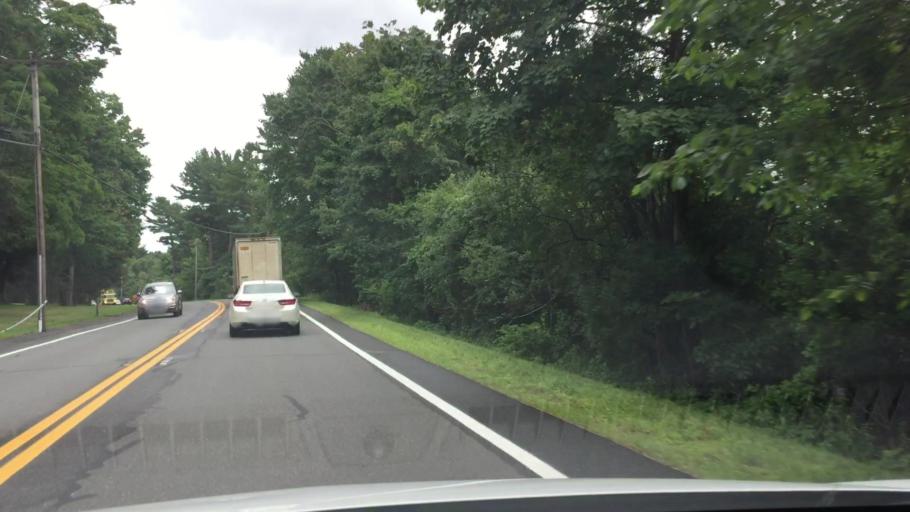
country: US
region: Massachusetts
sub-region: Berkshire County
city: Lenox
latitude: 42.3389
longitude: -73.2683
